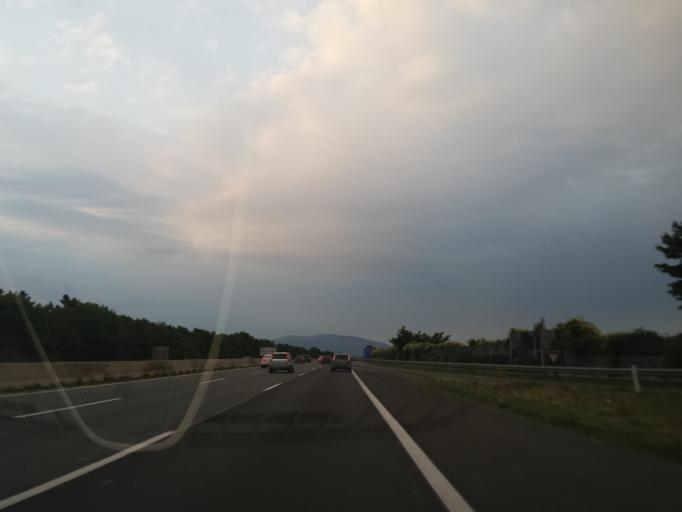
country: AT
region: Lower Austria
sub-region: Politischer Bezirk Baden
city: Leobersdorf
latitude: 47.9378
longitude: 16.2119
